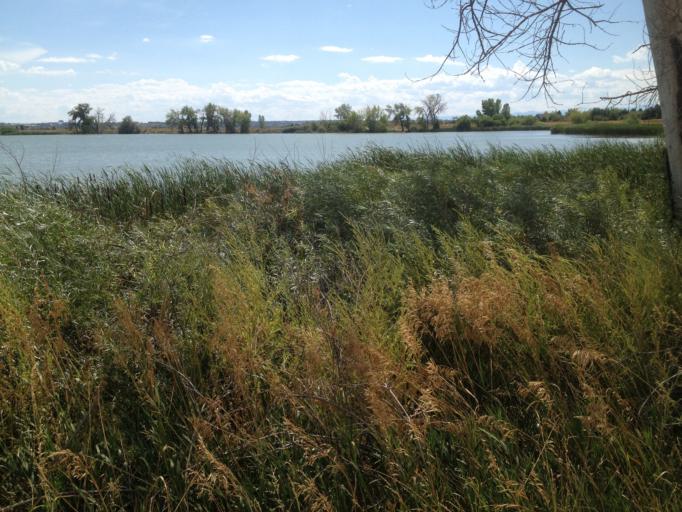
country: US
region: Colorado
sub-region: Adams County
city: Northglenn
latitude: 39.9554
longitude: -105.0146
